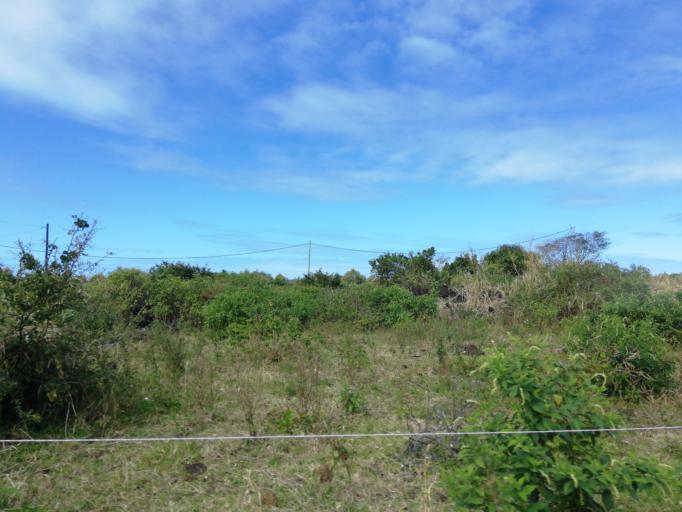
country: MU
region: Grand Port
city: Plaine Magnien
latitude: -20.4647
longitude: 57.6767
